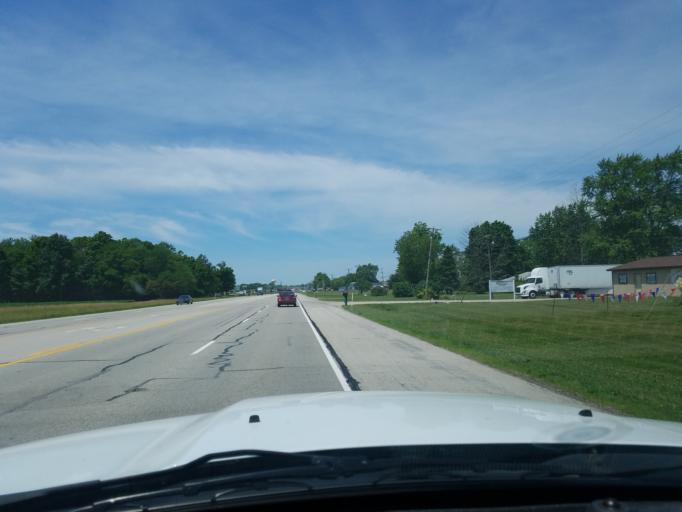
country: US
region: Indiana
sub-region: Delaware County
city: Daleville
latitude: 40.1135
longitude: -85.5497
